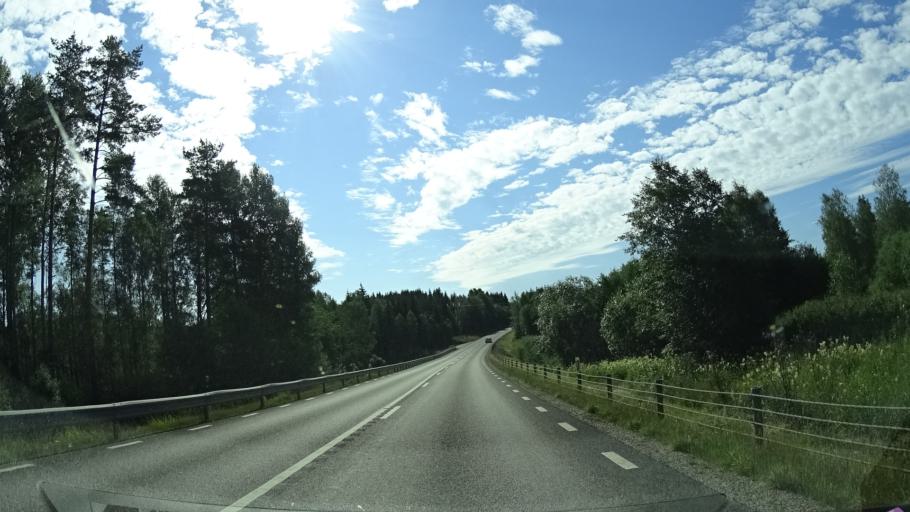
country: SE
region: Vaermland
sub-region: Arjangs Kommun
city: Toecksfors
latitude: 59.4858
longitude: 11.9452
